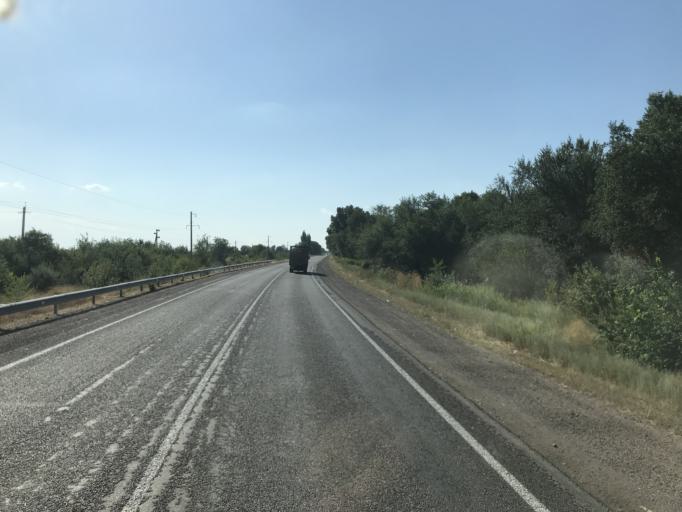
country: KZ
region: Zhambyl
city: Georgiyevka
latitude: 43.1910
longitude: 74.5404
